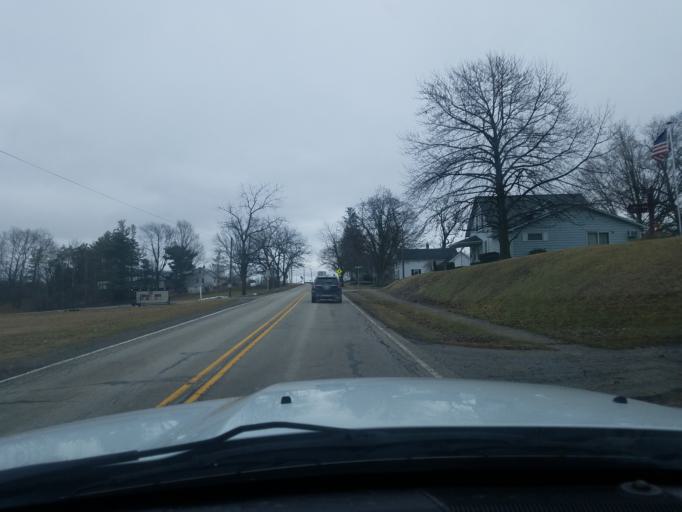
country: US
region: Indiana
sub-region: Noble County
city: Albion
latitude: 41.3958
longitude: -85.4173
